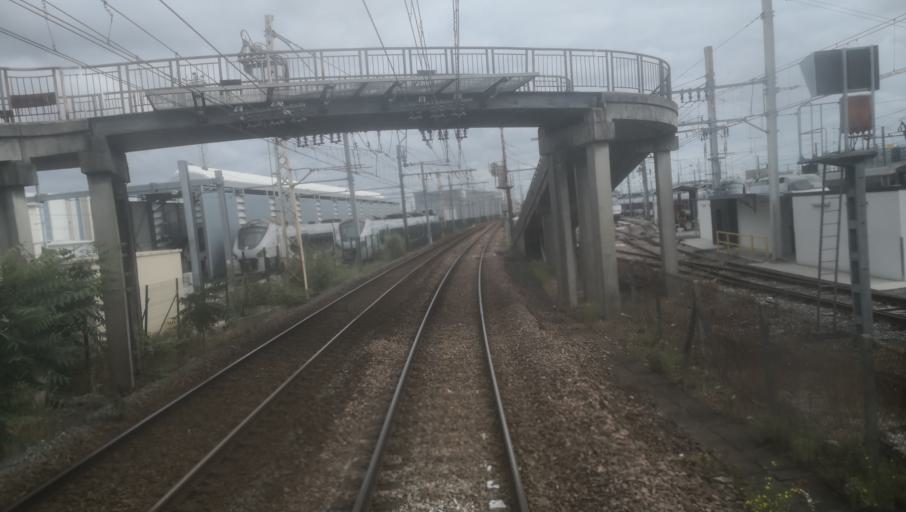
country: FR
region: Aquitaine
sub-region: Departement de la Gironde
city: Begles
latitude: 44.8150
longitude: -0.5599
